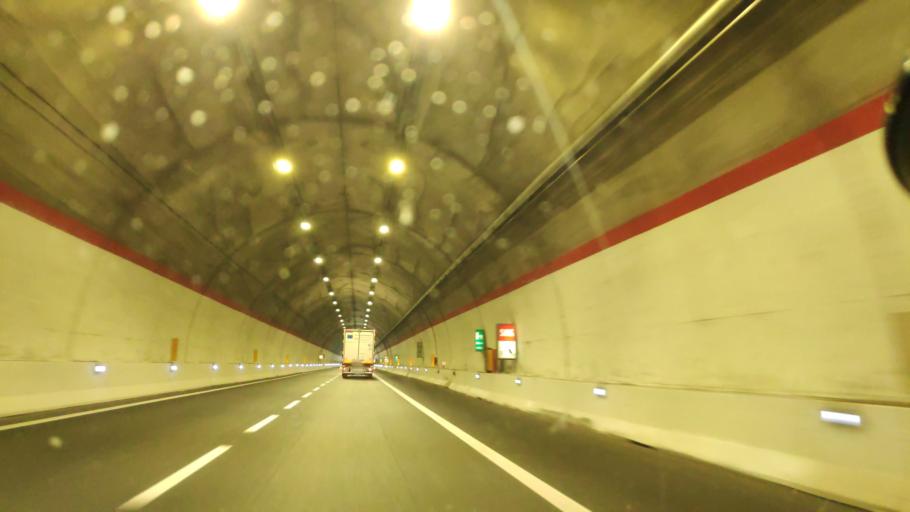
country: IT
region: Campania
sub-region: Provincia di Salerno
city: Sicignano degli Alburni
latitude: 40.5813
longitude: 15.3432
